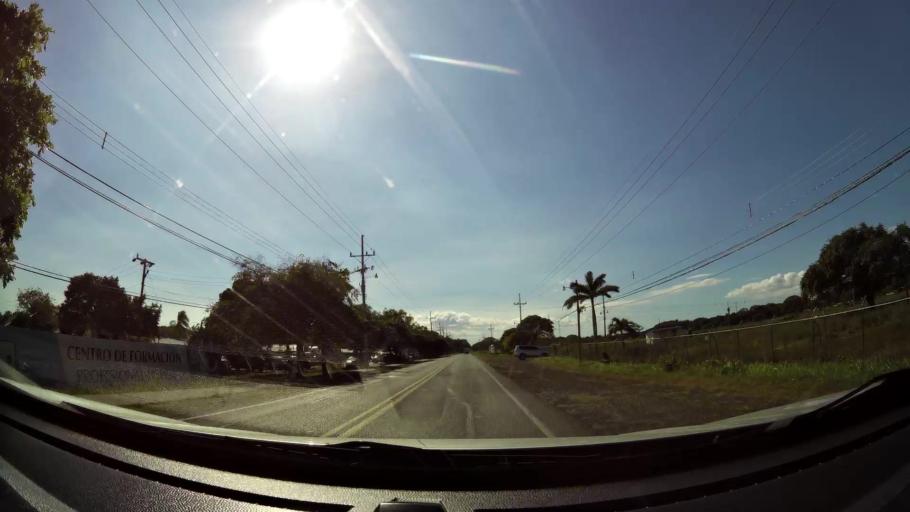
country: CR
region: Guanacaste
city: Liberia
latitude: 10.6205
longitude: -85.4570
